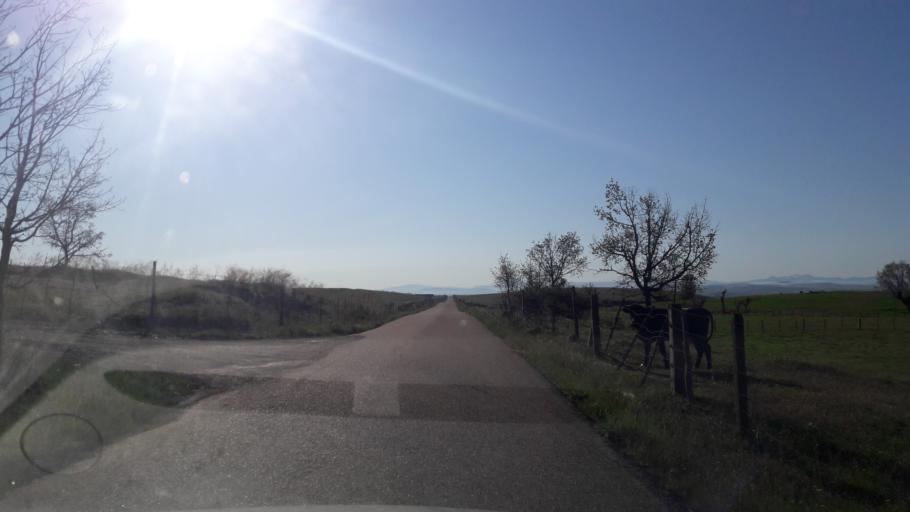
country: ES
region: Castille and Leon
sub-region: Provincia de Salamanca
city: Herguijuela del Campo
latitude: 40.6332
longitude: -5.8821
